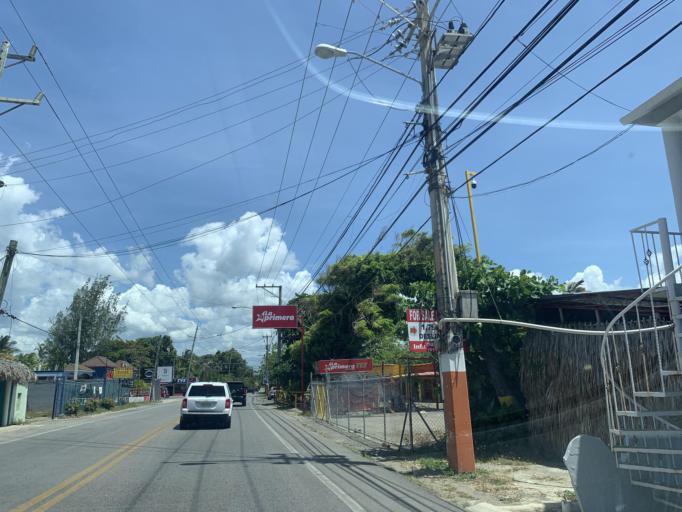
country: DO
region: Puerto Plata
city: Cabarete
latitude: 19.7350
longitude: -70.3894
